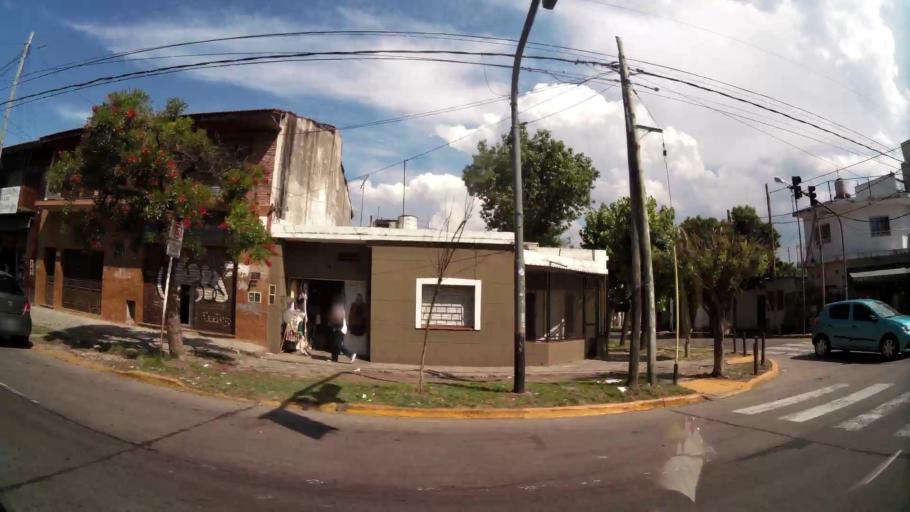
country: AR
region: Buenos Aires
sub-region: Partido de Tigre
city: Tigre
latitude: -34.4638
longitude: -58.5789
